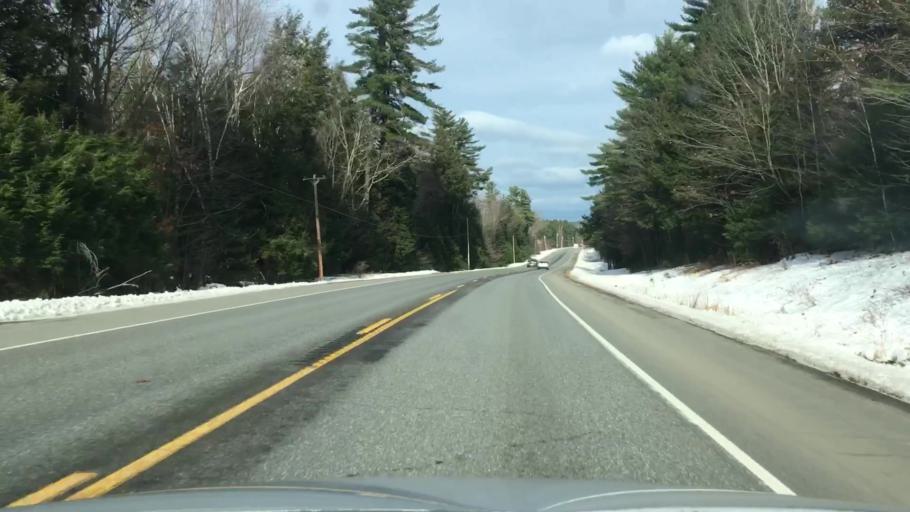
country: US
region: Maine
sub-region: Kennebec County
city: Monmouth
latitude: 44.2483
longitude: -70.0654
